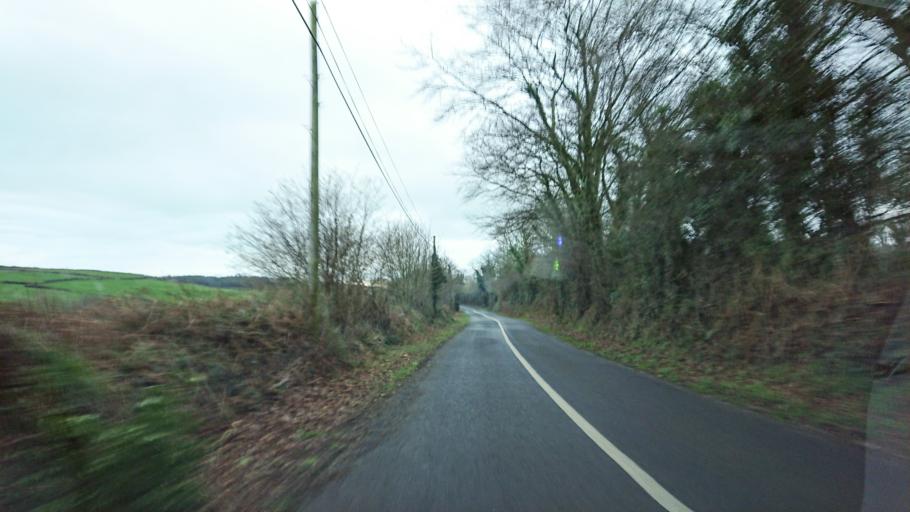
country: IE
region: Munster
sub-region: Waterford
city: Portlaw
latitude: 52.1646
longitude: -7.3882
